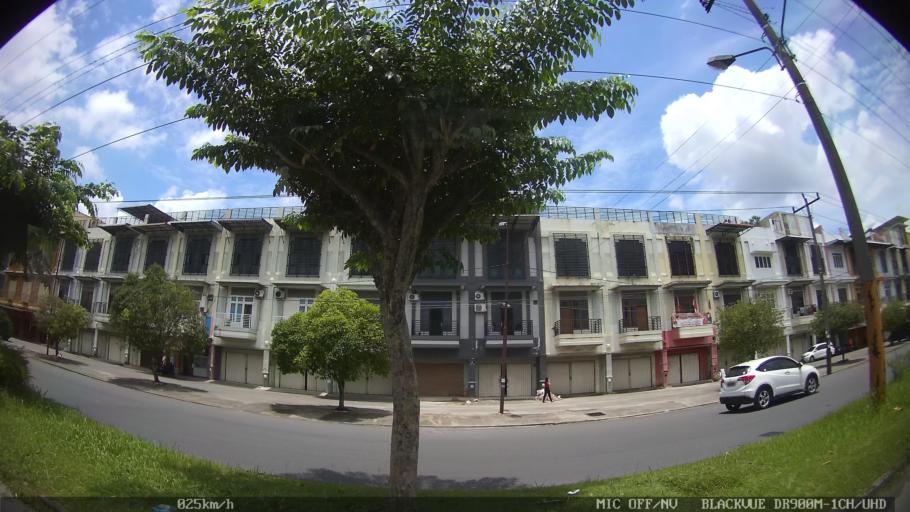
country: ID
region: North Sumatra
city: Medan
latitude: 3.6141
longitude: 98.7140
